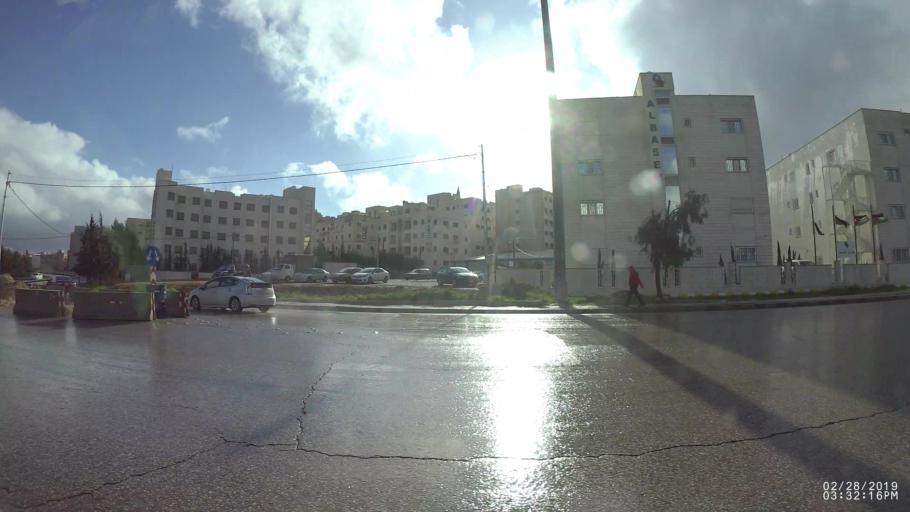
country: JO
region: Amman
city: Al Jubayhah
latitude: 32.0040
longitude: 35.8739
